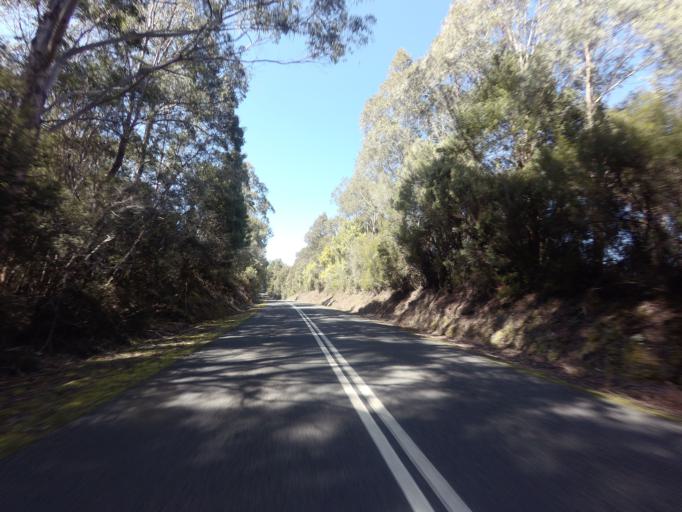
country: AU
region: Tasmania
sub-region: Derwent Valley
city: New Norfolk
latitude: -42.7539
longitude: 146.5245
